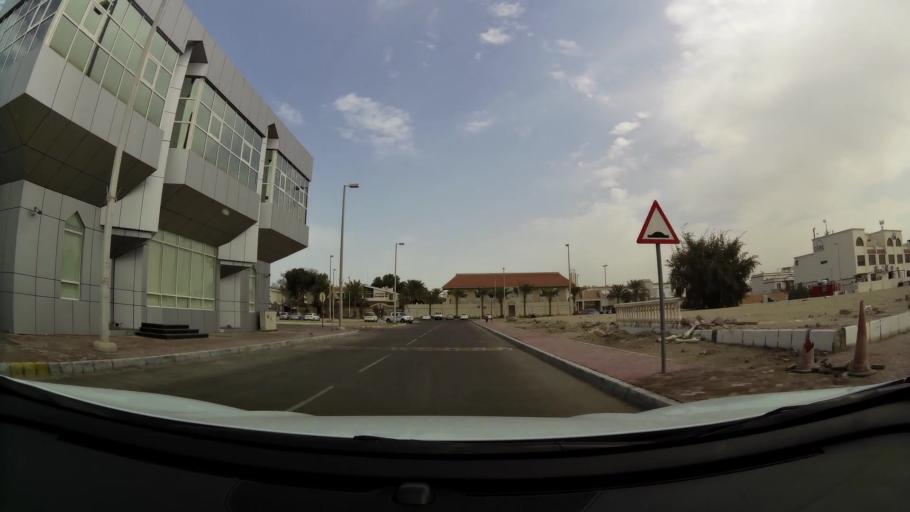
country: AE
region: Abu Dhabi
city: Abu Dhabi
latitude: 24.4596
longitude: 54.3480
